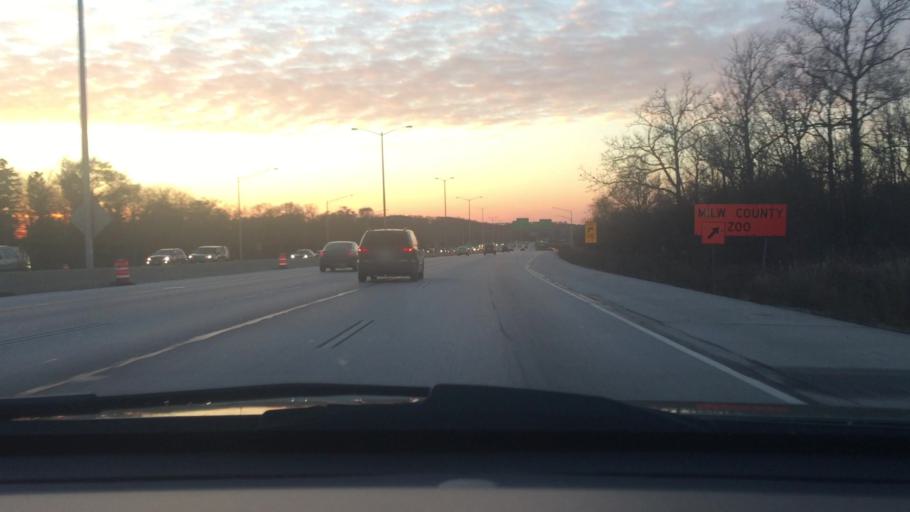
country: US
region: Wisconsin
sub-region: Waukesha County
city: Elm Grove
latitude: 43.0246
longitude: -88.0985
